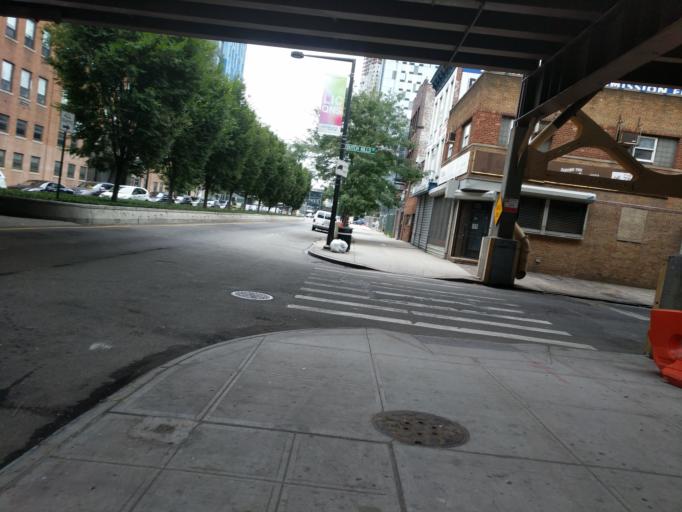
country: US
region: New York
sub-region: Queens County
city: Long Island City
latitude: 40.7477
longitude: -73.9407
